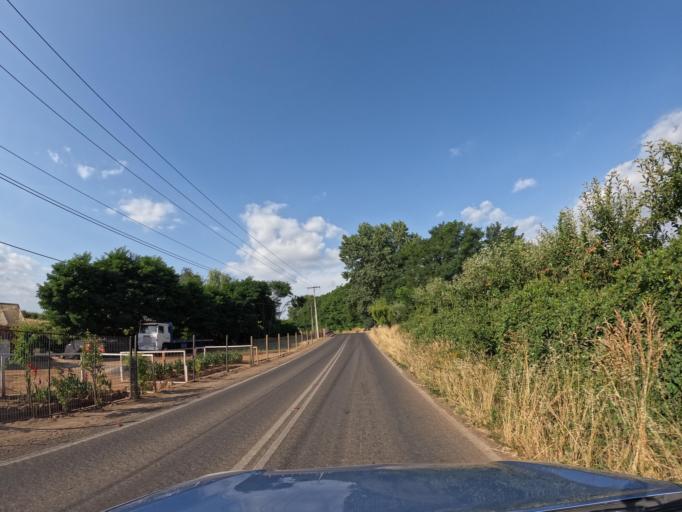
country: CL
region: Maule
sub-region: Provincia de Curico
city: Molina
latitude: -35.2687
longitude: -71.2464
